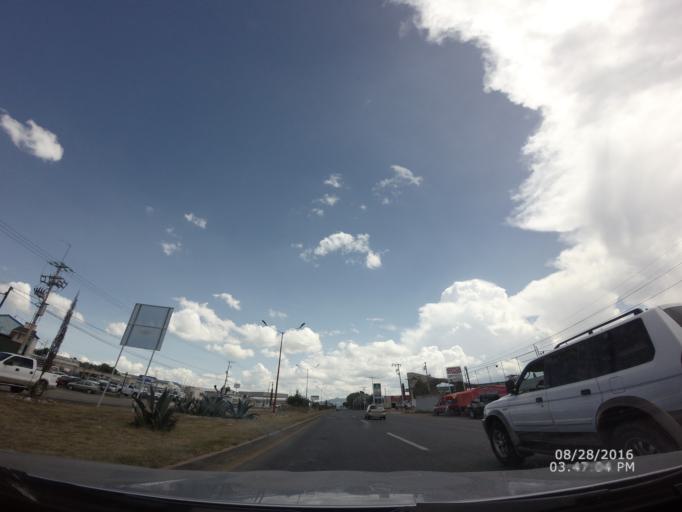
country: MX
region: Hidalgo
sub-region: Mineral de la Reforma
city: Nuevo Centro de Poblacion Agricola el Chacon
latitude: 20.0690
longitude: -98.7445
